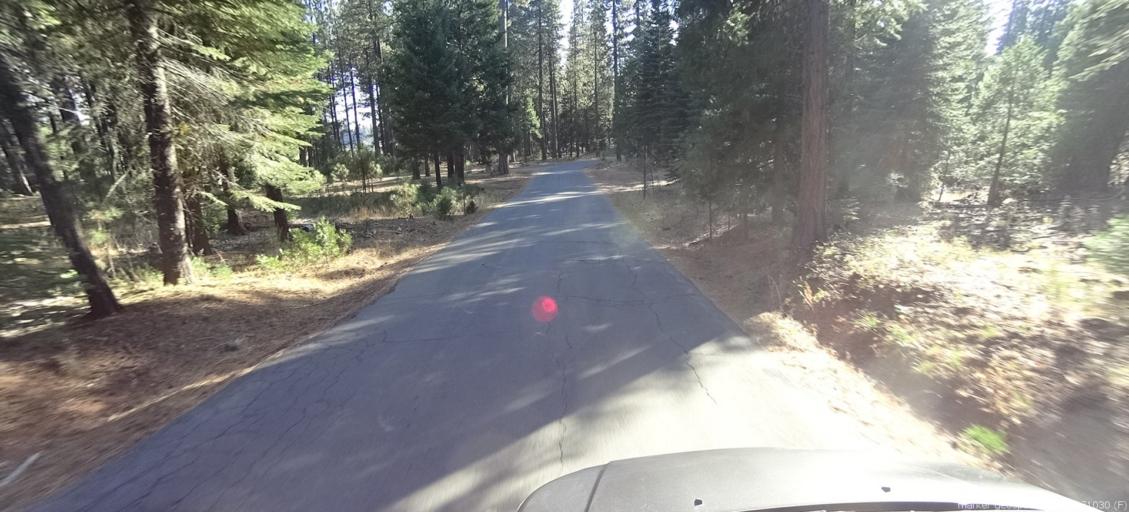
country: US
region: California
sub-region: Shasta County
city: Shingletown
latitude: 40.5472
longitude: -121.7340
